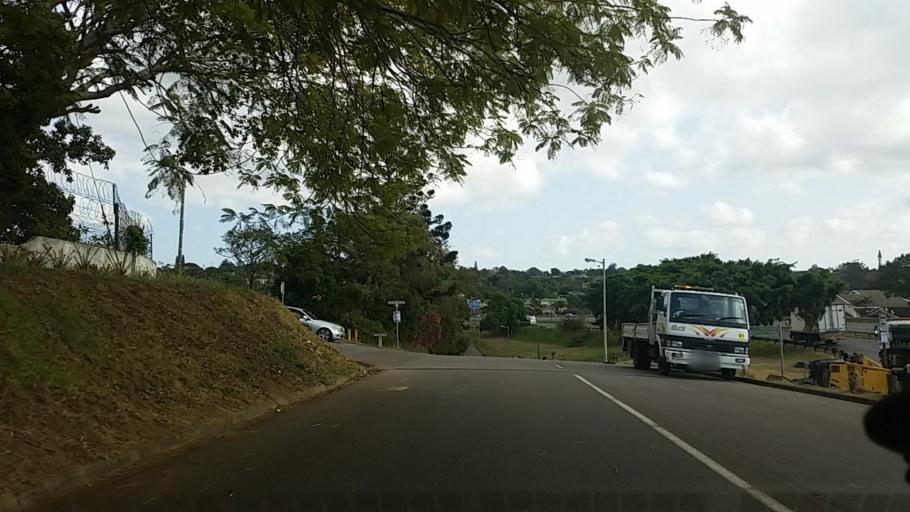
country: ZA
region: KwaZulu-Natal
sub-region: eThekwini Metropolitan Municipality
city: Berea
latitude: -29.8305
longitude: 30.9464
